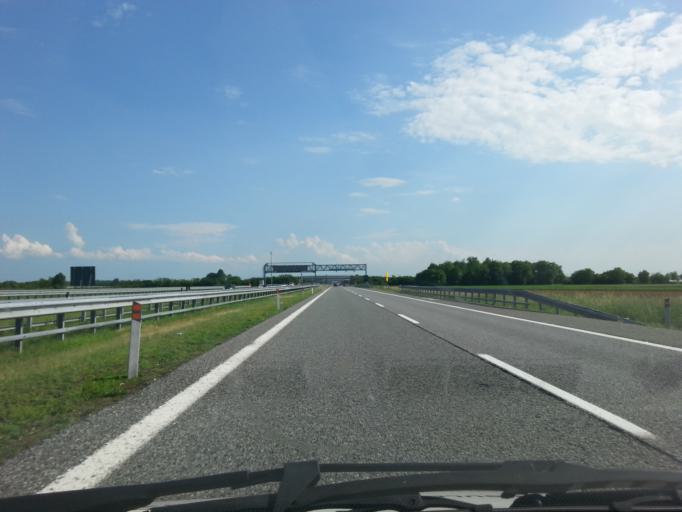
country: IT
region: Piedmont
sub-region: Provincia di Torino
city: Carmagnola
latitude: 44.8428
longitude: 7.7493
